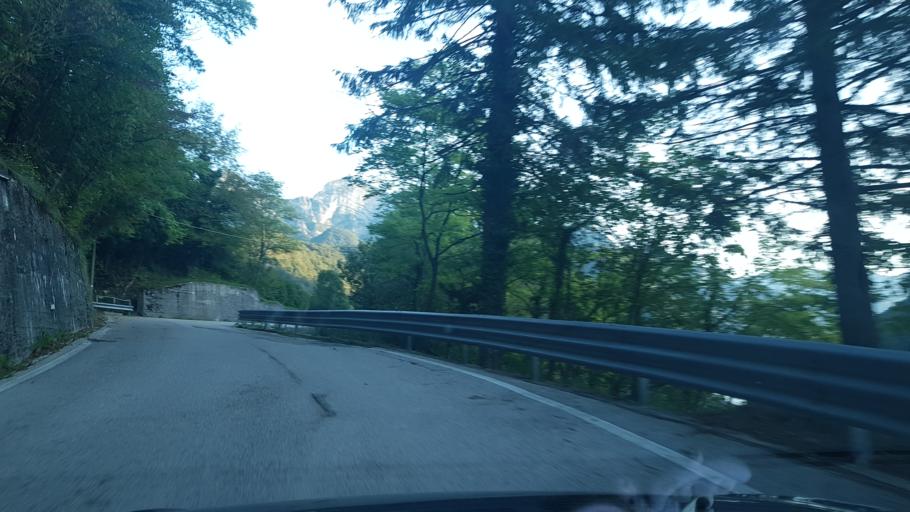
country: IT
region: Friuli Venezia Giulia
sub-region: Provincia di Pordenone
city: Frisanco
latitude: 46.2464
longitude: 12.7459
